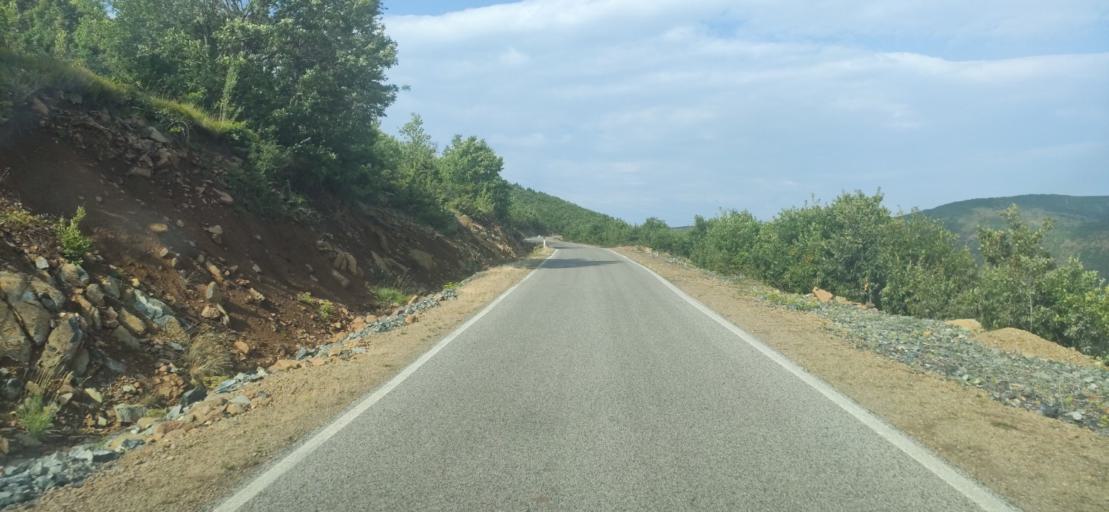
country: AL
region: Shkoder
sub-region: Rrethi i Pukes
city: Iballe
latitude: 42.1762
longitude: 20.0015
